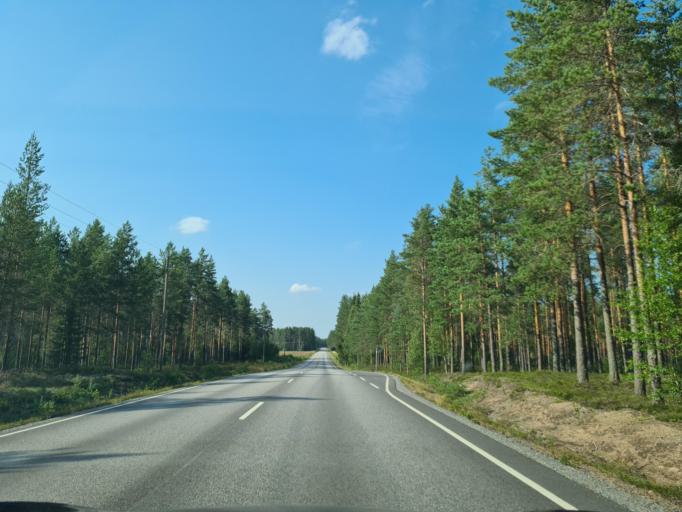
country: FI
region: Satakunta
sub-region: Pohjois-Satakunta
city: Karvia
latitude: 62.0646
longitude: 22.5106
